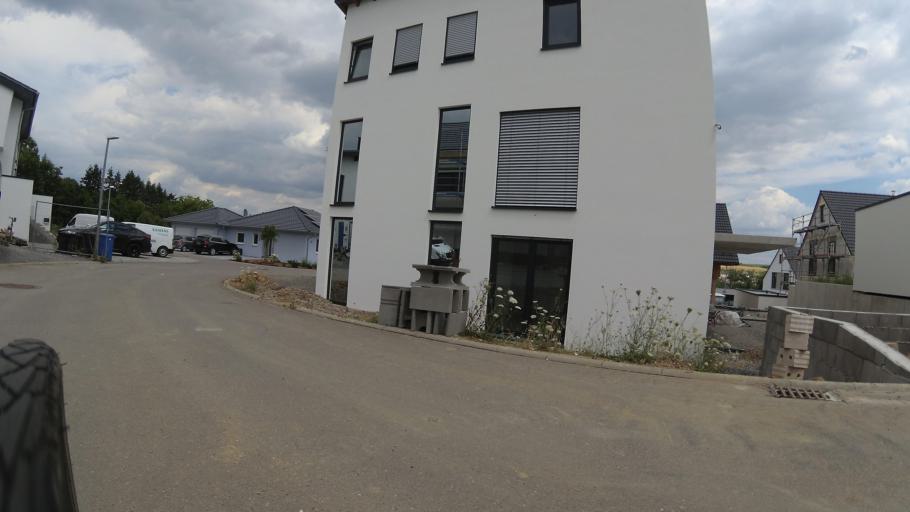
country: DE
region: Baden-Wuerttemberg
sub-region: Regierungsbezirk Stuttgart
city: Neudenau
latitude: 49.2825
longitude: 9.2512
